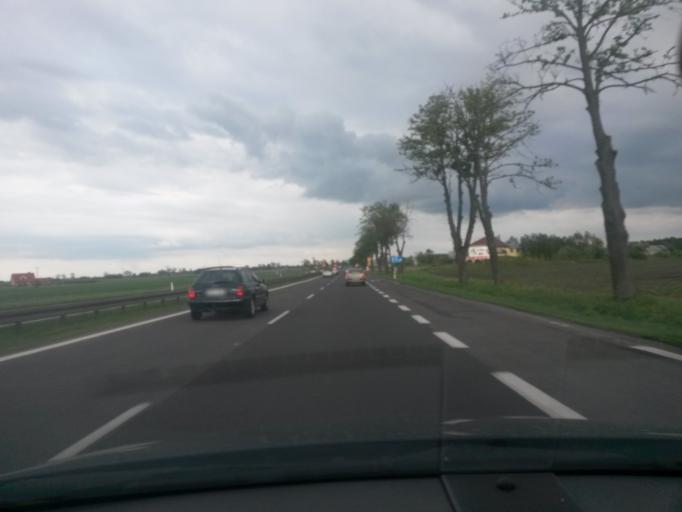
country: PL
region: Masovian Voivodeship
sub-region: Powiat plonski
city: Plonsk
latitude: 52.5968
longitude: 20.4257
